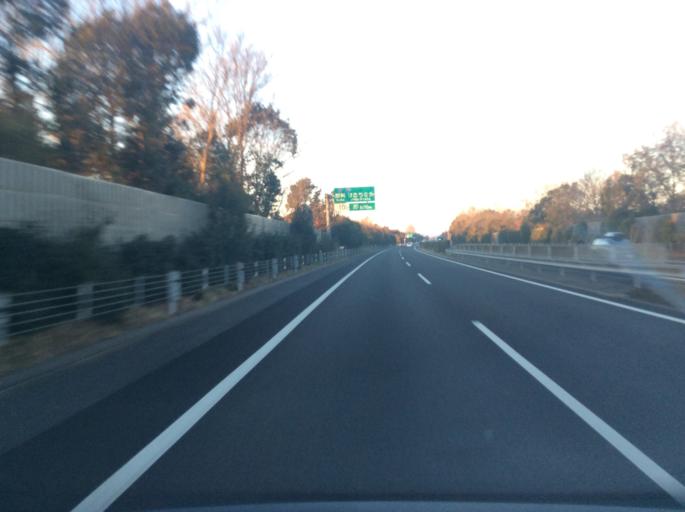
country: JP
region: Ibaraki
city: Hitachi-Naka
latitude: 36.4563
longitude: 140.4808
